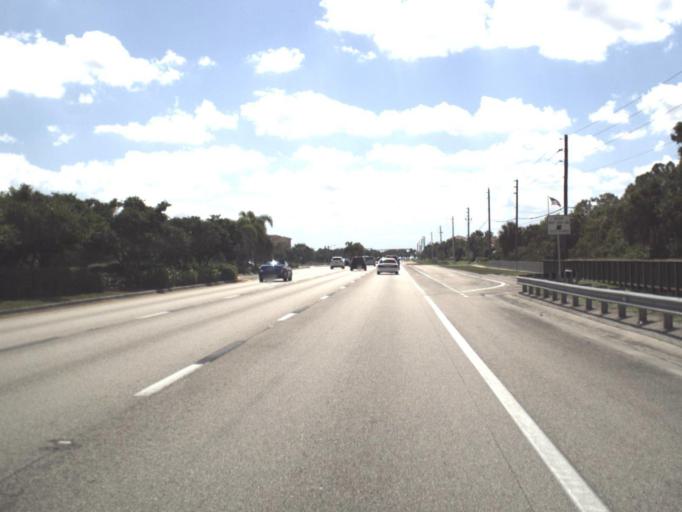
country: US
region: Florida
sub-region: Lee County
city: Estero
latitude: 26.4097
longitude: -81.8118
